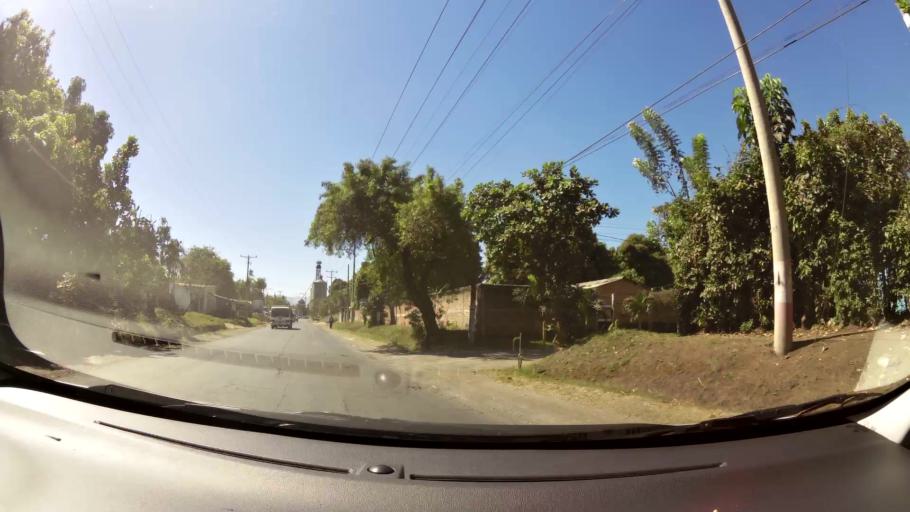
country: SV
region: La Libertad
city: San Juan Opico
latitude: 13.7837
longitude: -89.3721
